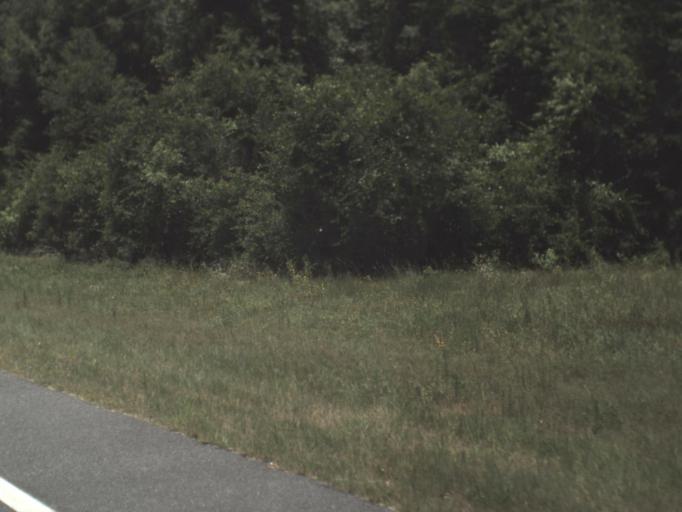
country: US
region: Florida
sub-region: Dixie County
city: Cross City
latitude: 29.6476
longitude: -82.9837
